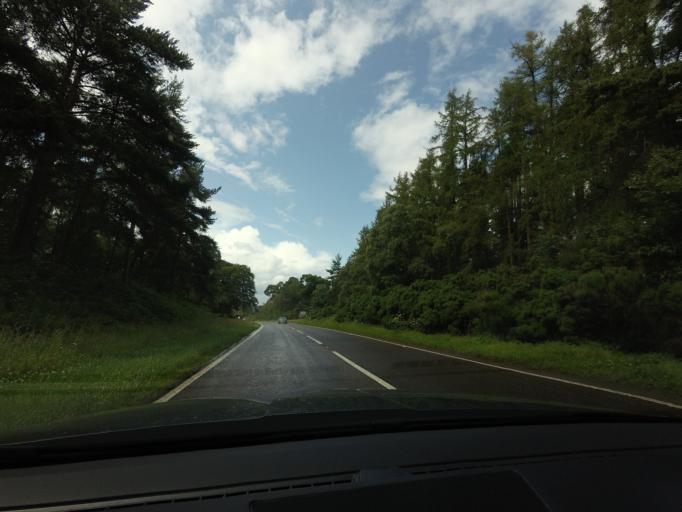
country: GB
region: Scotland
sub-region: Moray
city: Lhanbryd
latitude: 57.6335
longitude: -3.1869
